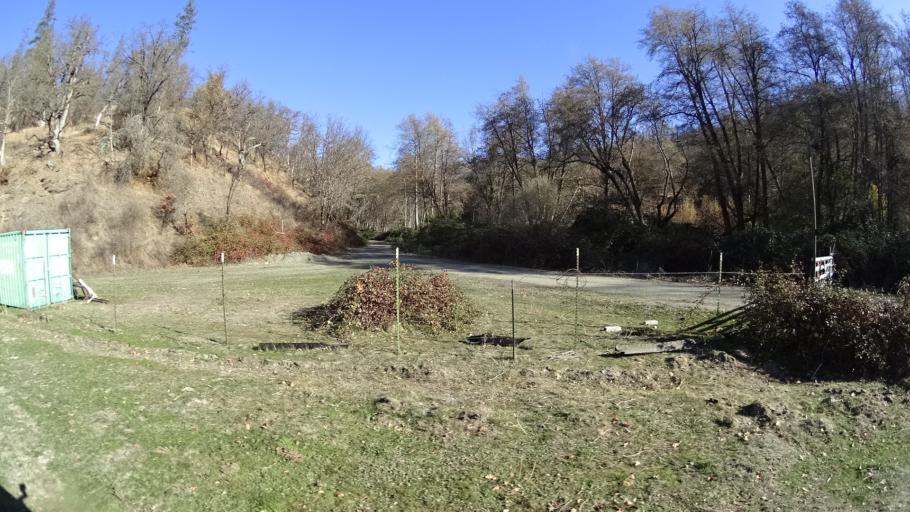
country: US
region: California
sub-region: Siskiyou County
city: Happy Camp
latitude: 41.8377
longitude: -123.0075
